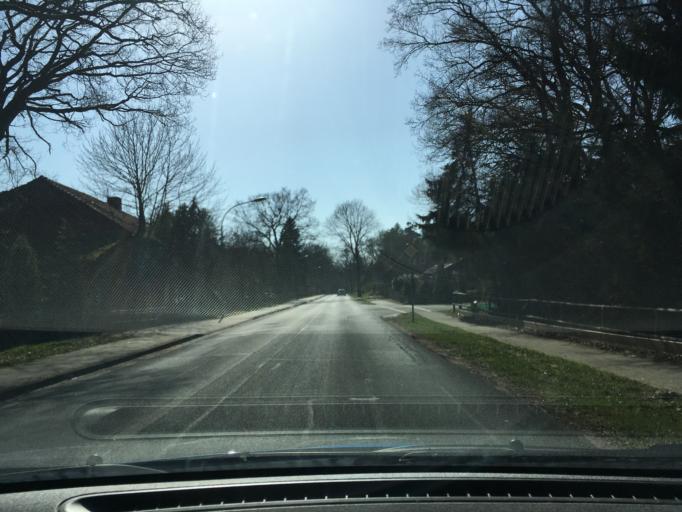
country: DE
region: Lower Saxony
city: Fassberg
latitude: 52.8276
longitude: 10.2097
